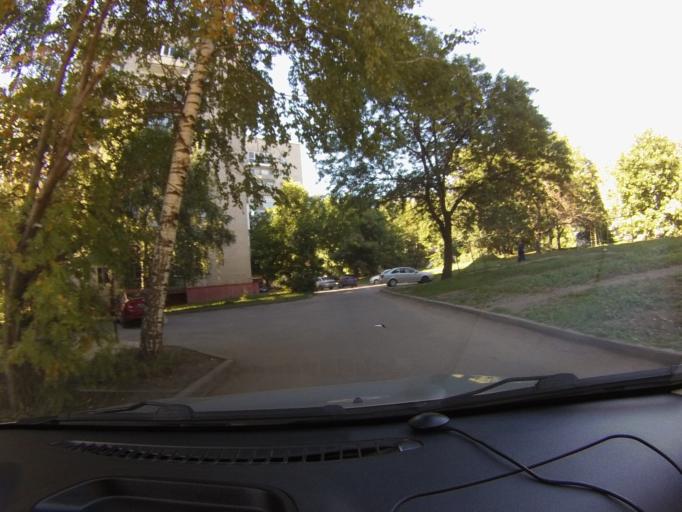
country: RU
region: Tambov
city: Tambov
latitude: 52.7590
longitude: 41.4061
